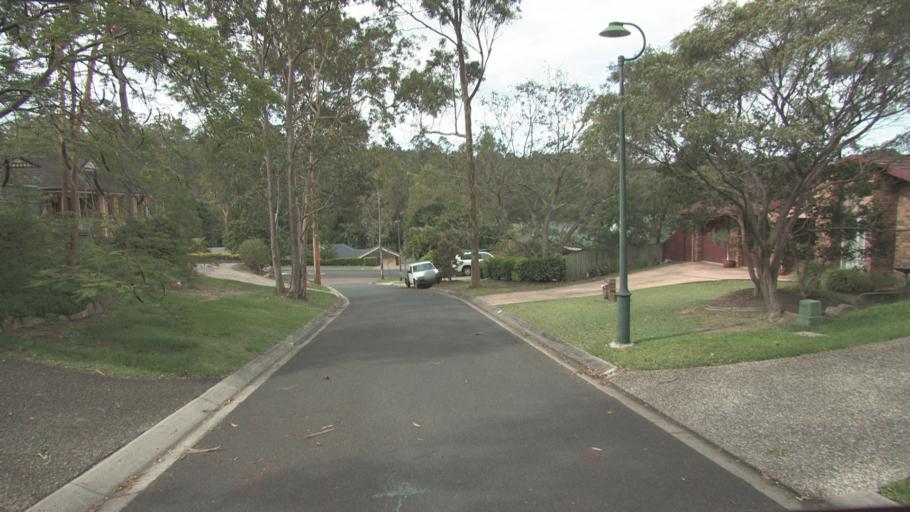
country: AU
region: Queensland
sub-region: Logan
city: Slacks Creek
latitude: -27.6579
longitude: 153.1965
